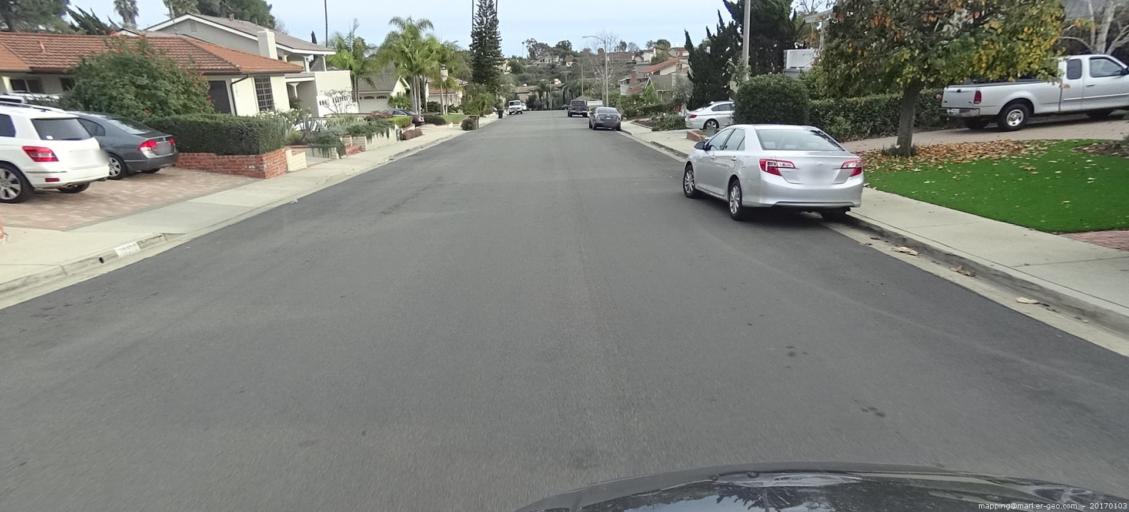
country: US
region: California
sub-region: Orange County
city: Dana Point
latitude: 33.4785
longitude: -117.6926
